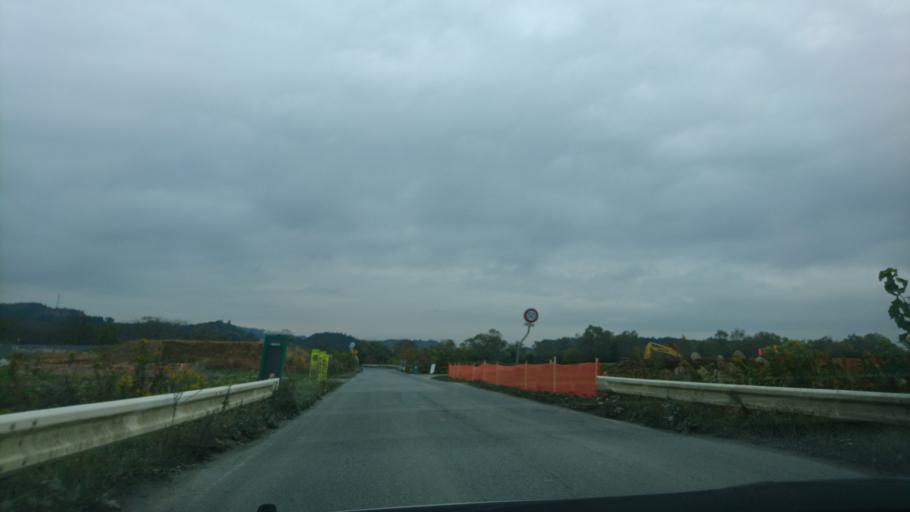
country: JP
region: Iwate
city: Ichinoseki
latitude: 38.9522
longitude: 141.1690
